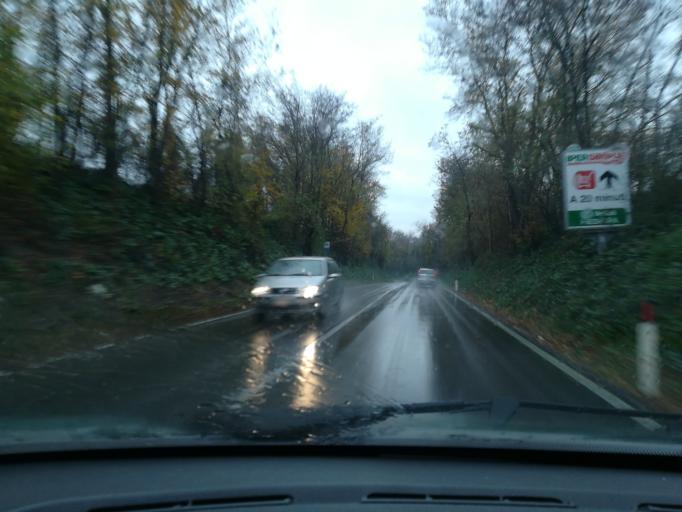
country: IT
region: The Marches
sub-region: Provincia di Macerata
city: Sforzacosta
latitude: 43.2650
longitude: 13.4216
